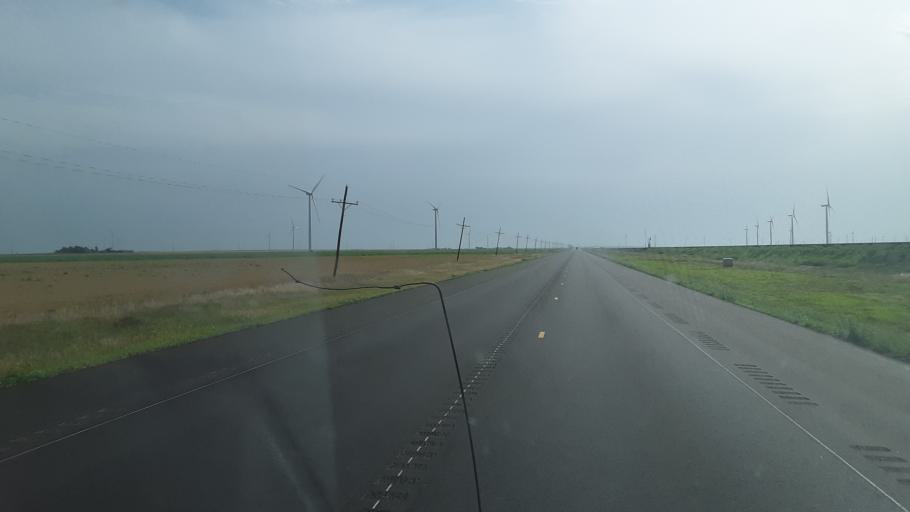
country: US
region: Kansas
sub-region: Ford County
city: Dodge City
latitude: 37.8051
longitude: -99.8482
